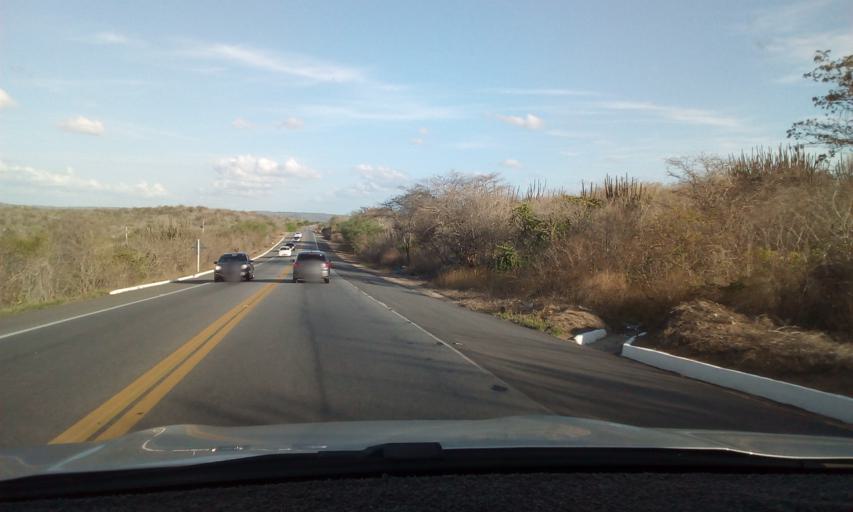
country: BR
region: Paraiba
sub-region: Pocinhos
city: Pocinhos
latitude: -7.1597
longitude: -36.0792
